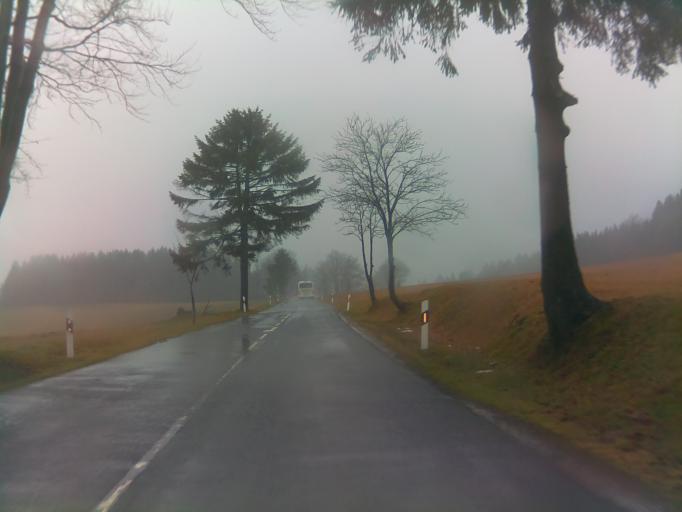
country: DE
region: Thuringia
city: Masserberg
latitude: 50.5109
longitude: 10.9187
